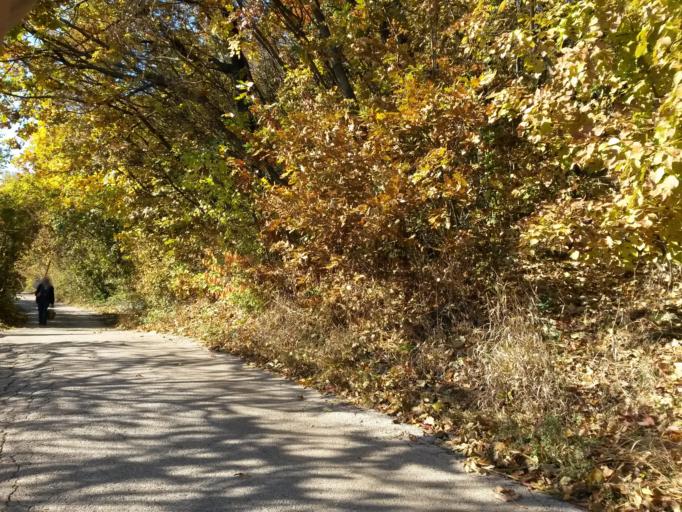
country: HU
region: Pest
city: Budaors
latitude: 47.4776
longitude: 18.9722
